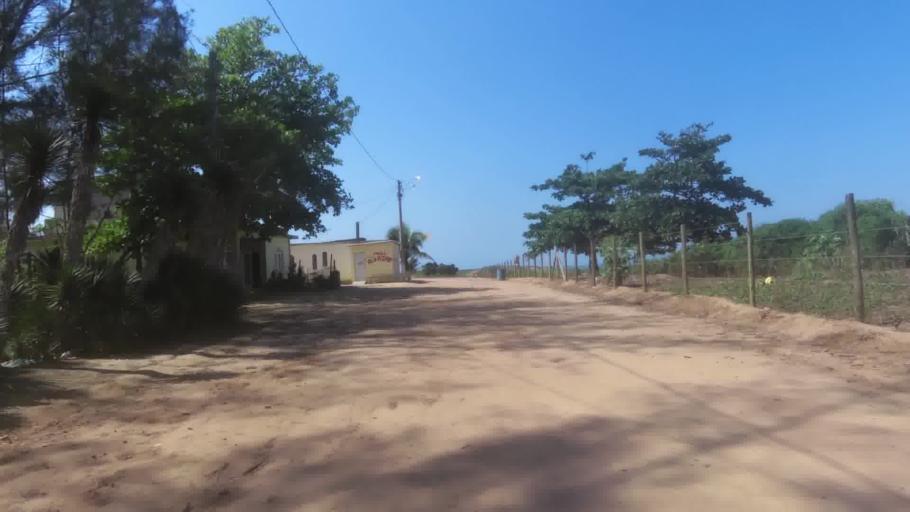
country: BR
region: Espirito Santo
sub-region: Marataizes
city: Marataizes
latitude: -21.1132
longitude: -40.8554
